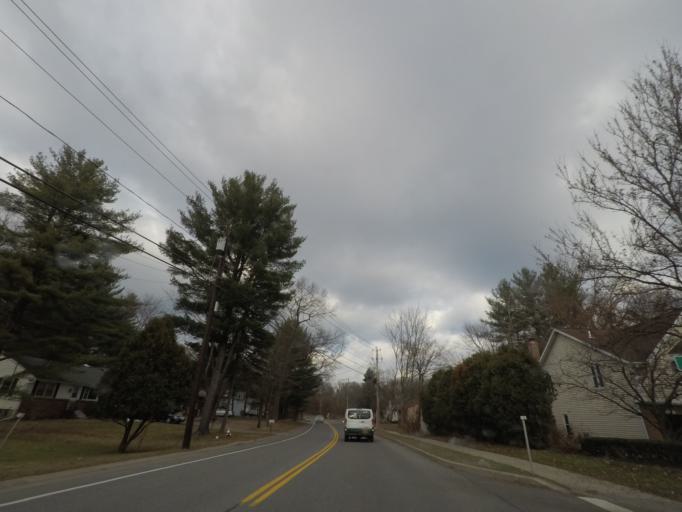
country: US
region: New York
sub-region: Albany County
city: Westmere
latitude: 42.6787
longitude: -73.8730
